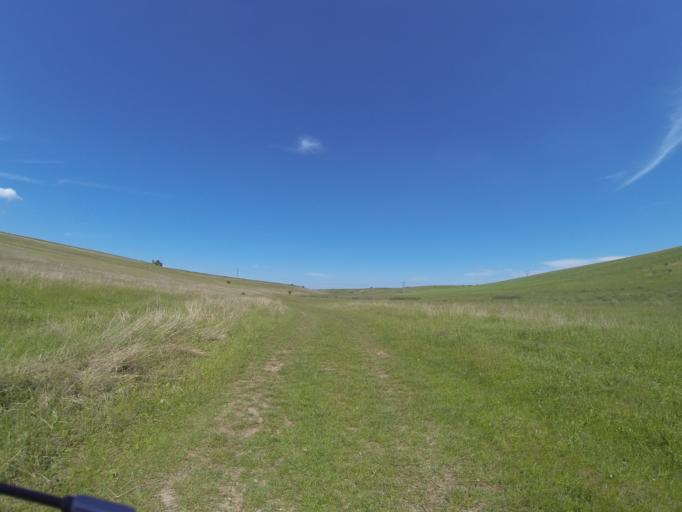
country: RO
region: Dolj
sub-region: Comuna Leu
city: Leu
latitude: 44.2474
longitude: 24.0024
